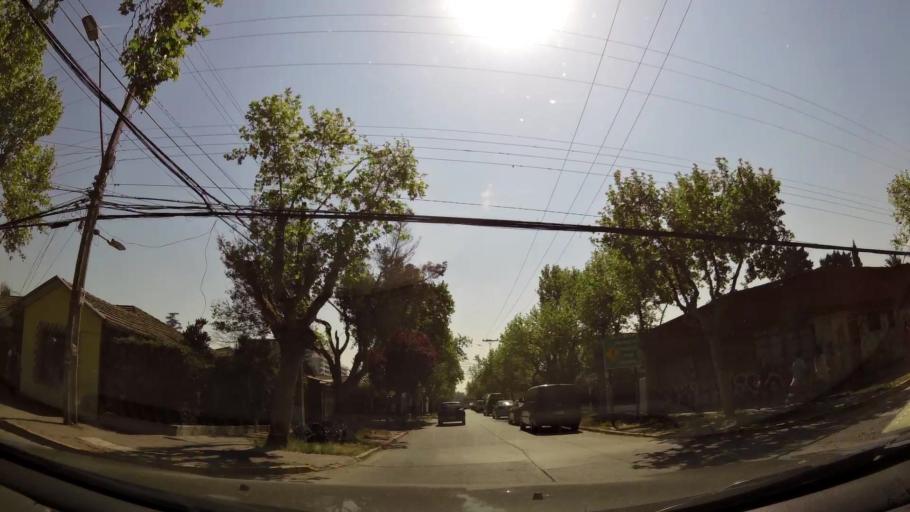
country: CL
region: Santiago Metropolitan
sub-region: Provincia de Maipo
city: San Bernardo
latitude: -33.5939
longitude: -70.7087
